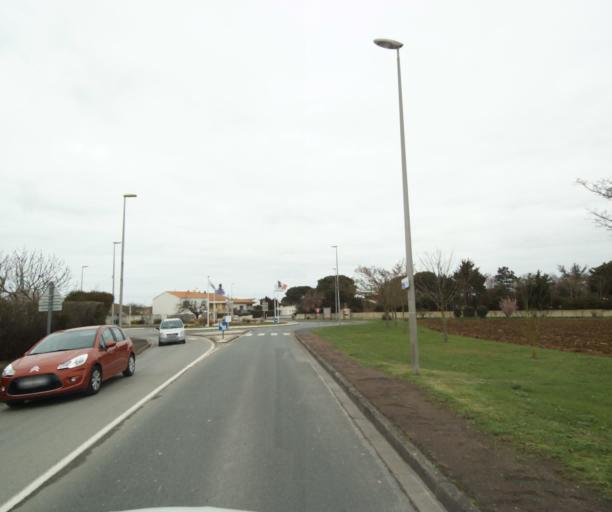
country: FR
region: Poitou-Charentes
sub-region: Departement de la Charente-Maritime
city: Nieul-sur-Mer
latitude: 46.1998
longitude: -1.1599
